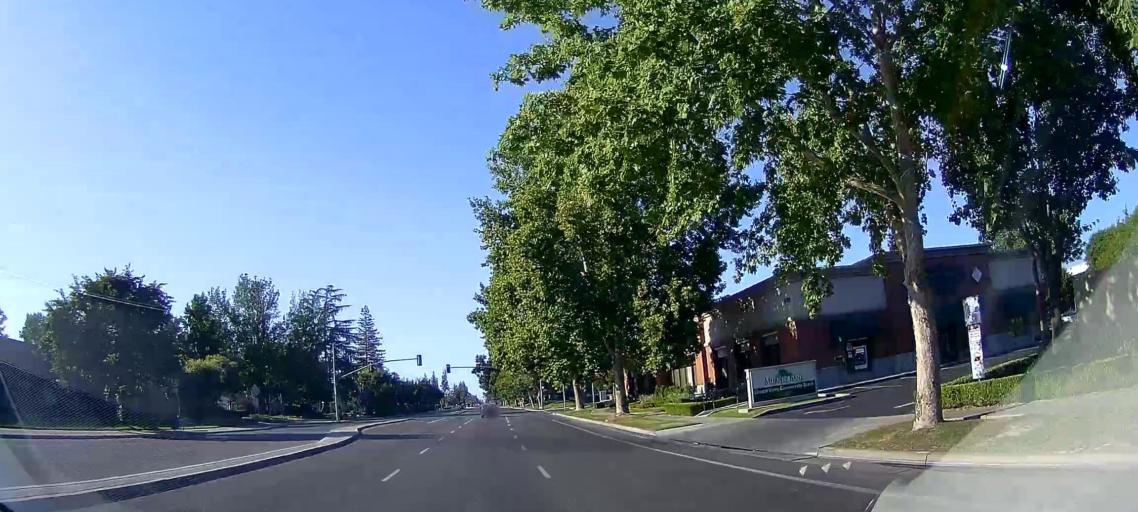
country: US
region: California
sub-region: Fresno County
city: Fresno
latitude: 36.8111
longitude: -119.8084
